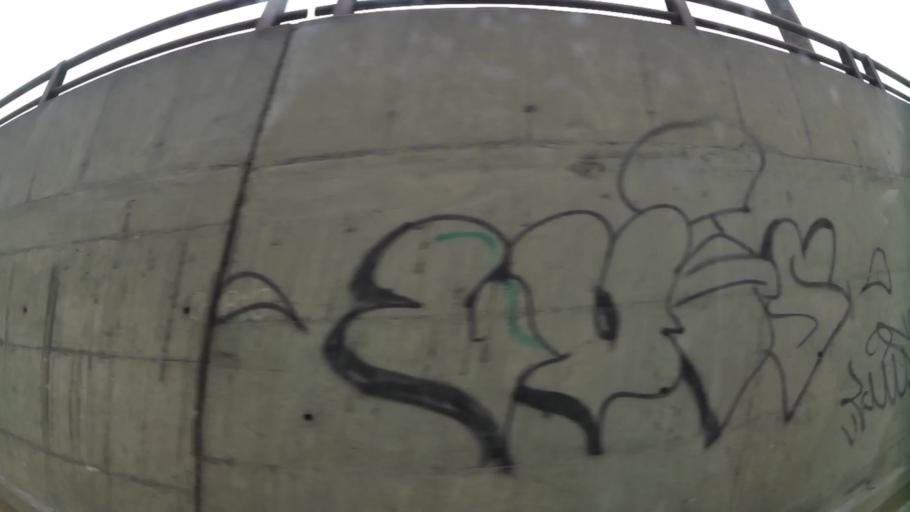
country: PE
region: Lima
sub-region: Lima
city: Santa Maria
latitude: -12.0177
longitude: -76.8944
